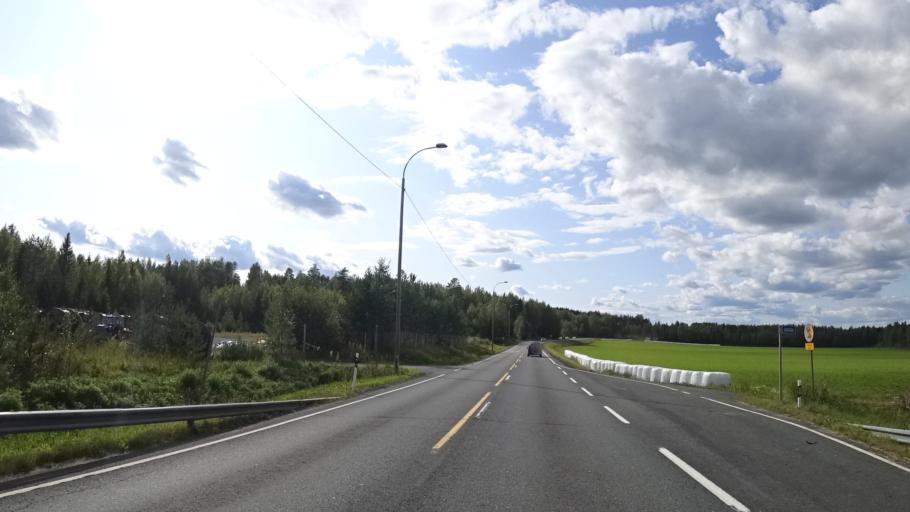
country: FI
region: North Karelia
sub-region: Keski-Karjala
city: Tohmajaervi
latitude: 62.1899
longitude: 30.4442
